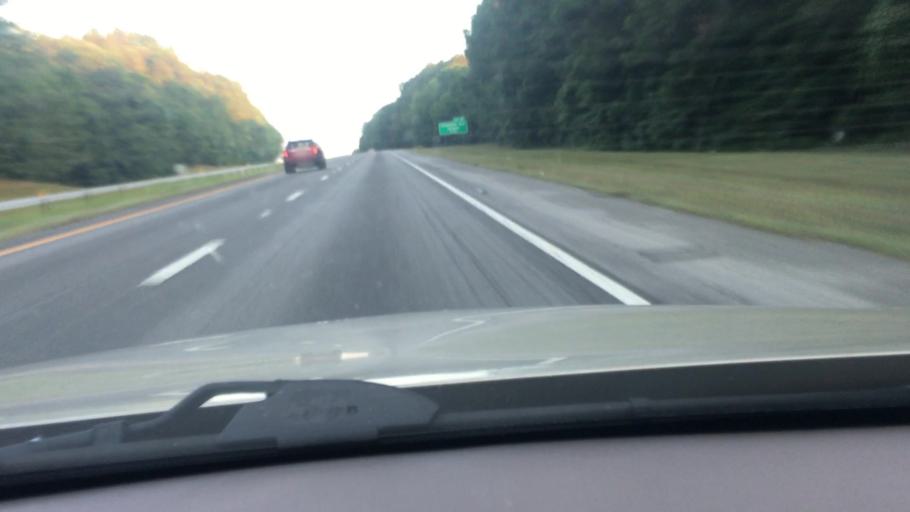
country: US
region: South Carolina
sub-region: Lexington County
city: Chapin
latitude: 34.1703
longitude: -81.3012
